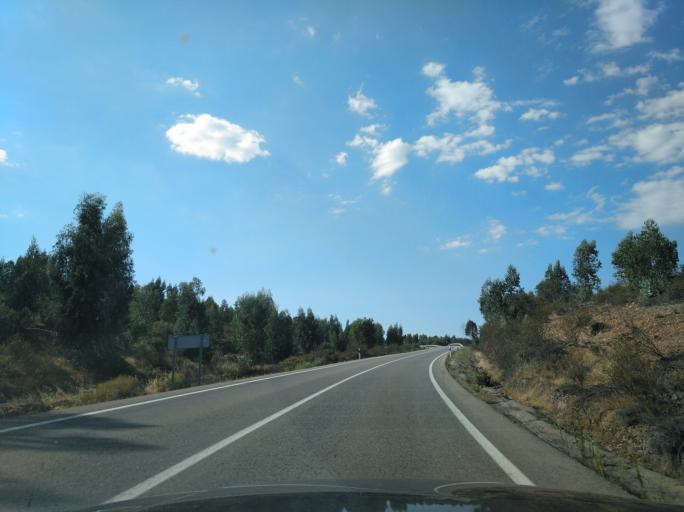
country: ES
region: Andalusia
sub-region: Provincia de Huelva
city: Santa Barbara de Casa
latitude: 37.8048
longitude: -7.2021
